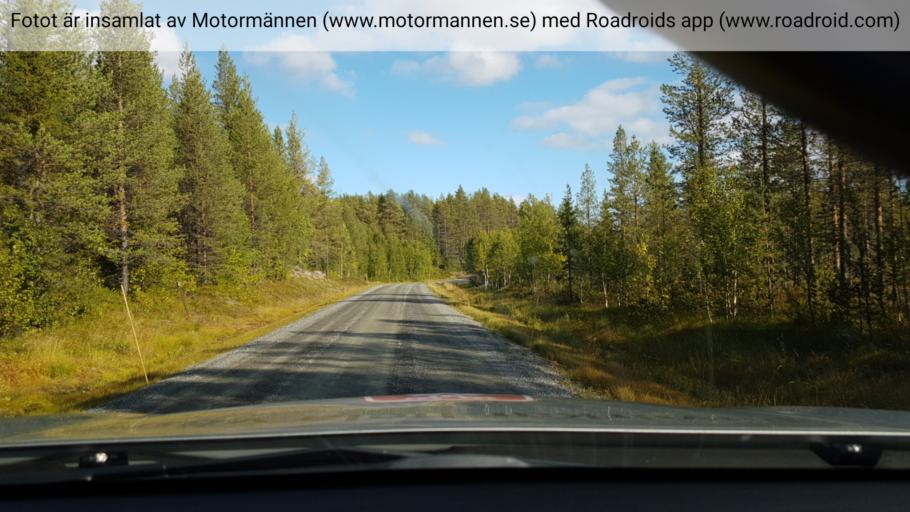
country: SE
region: Vaesterbotten
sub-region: Sorsele Kommun
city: Sorsele
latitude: 65.4803
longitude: 17.6011
